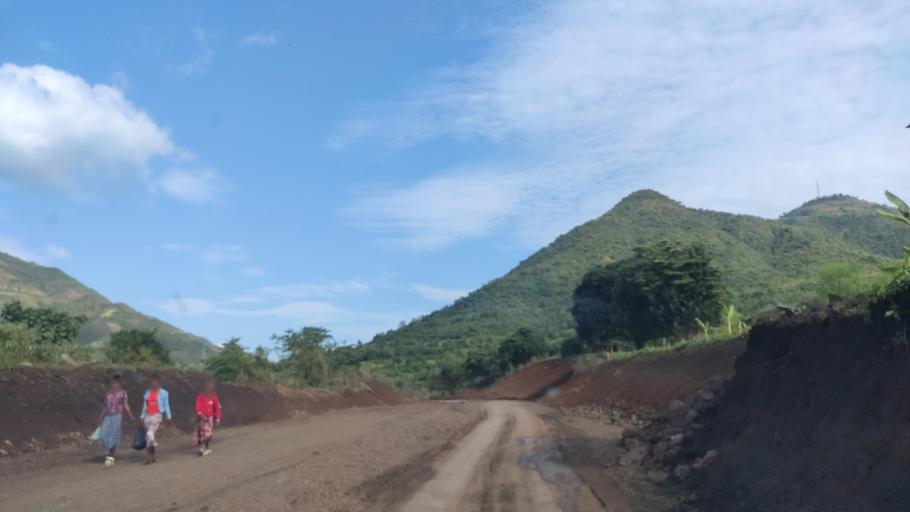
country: ET
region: Southern Nations, Nationalities, and People's Region
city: Arba Minch'
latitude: 6.4254
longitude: 37.3356
